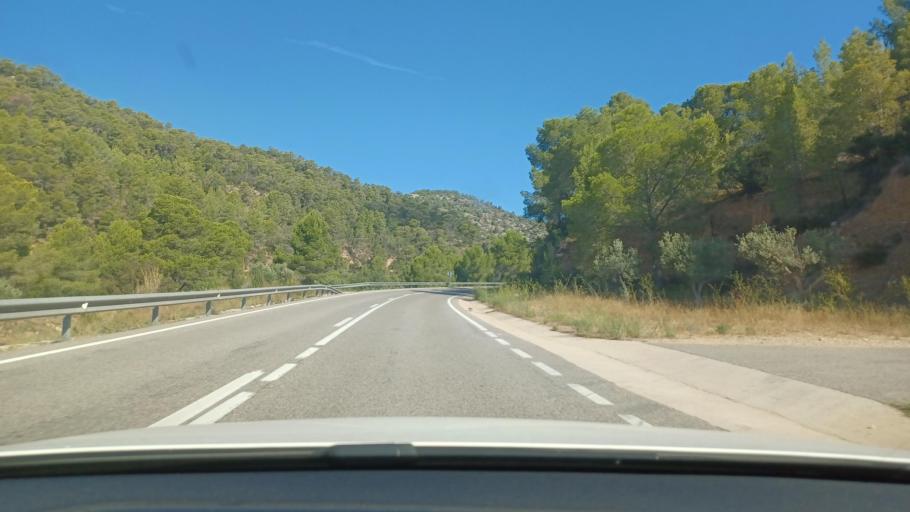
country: ES
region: Catalonia
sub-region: Provincia de Tarragona
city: Benifallet
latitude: 40.9533
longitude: 0.4471
